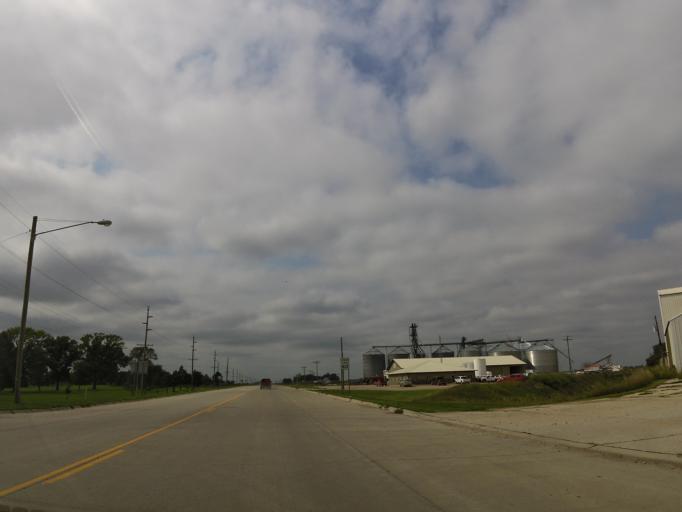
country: US
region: Minnesota
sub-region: Lac qui Parle County
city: Dawson
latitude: 44.9358
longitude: -96.0650
